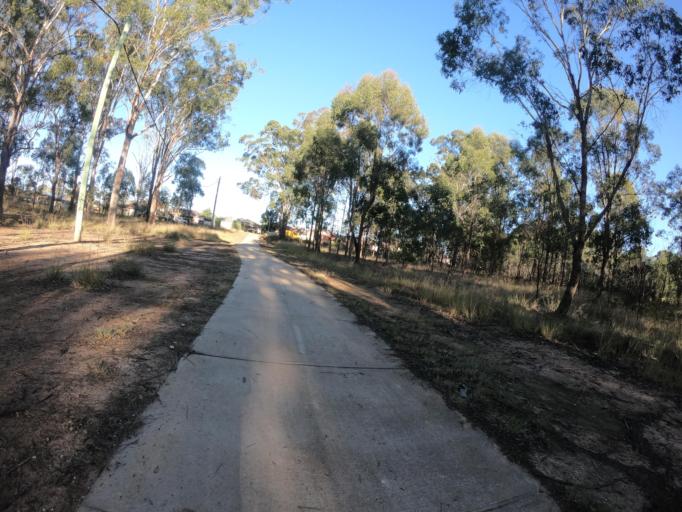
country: AU
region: New South Wales
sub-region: Hawkesbury
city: South Windsor
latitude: -33.6366
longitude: 150.8090
